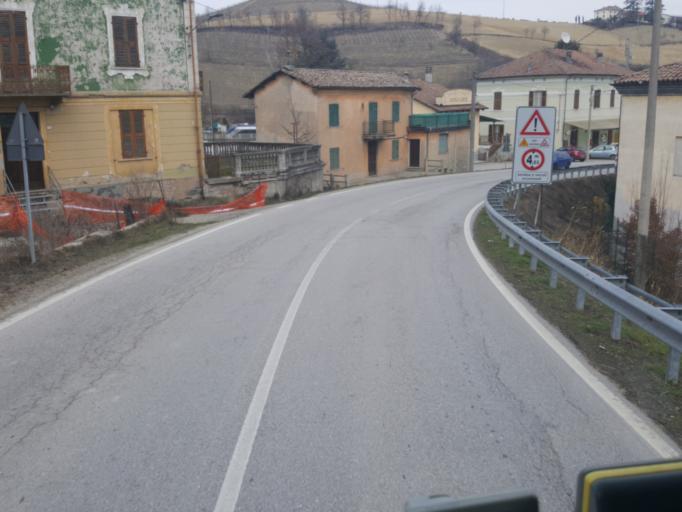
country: IT
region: Piedmont
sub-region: Provincia di Asti
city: Castelnuovo Belbo
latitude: 44.7761
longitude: 8.4003
